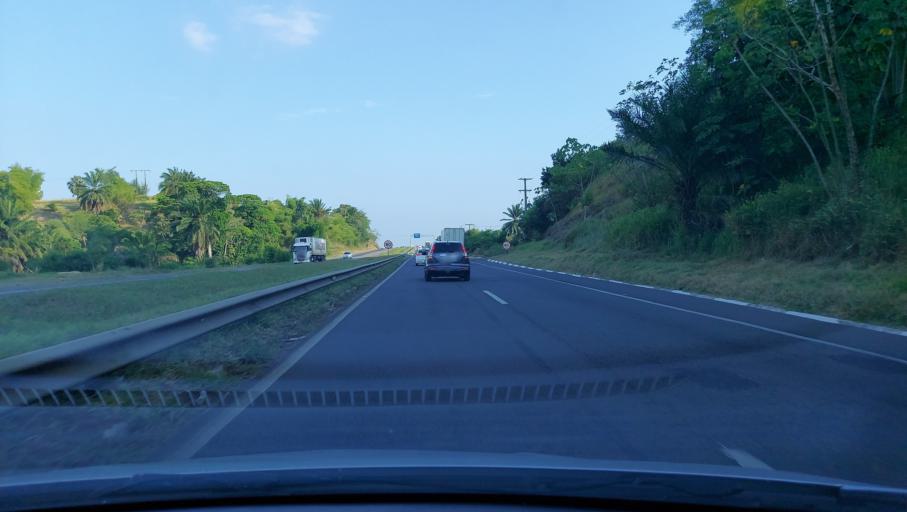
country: BR
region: Bahia
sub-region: Santo Amaro
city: Santo Amaro
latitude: -12.4453
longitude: -38.7167
